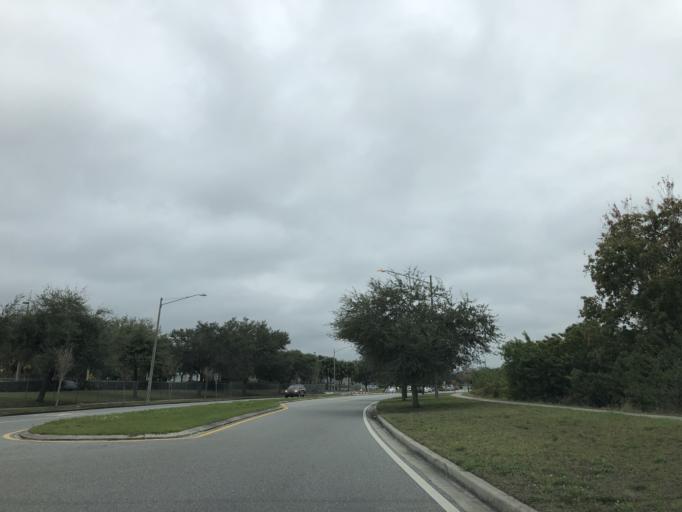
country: US
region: Florida
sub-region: Orange County
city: Hunters Creek
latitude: 28.3692
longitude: -81.3994
